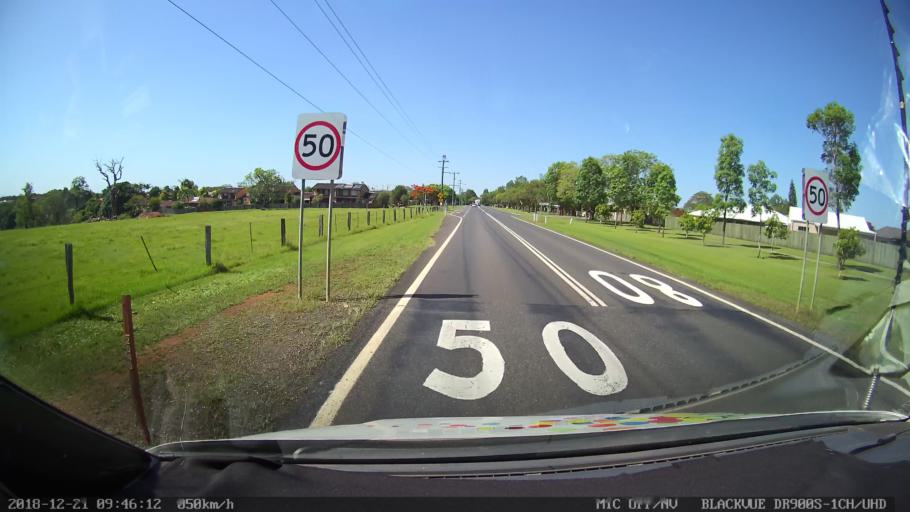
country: AU
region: New South Wales
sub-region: Clarence Valley
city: Grafton
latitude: -29.6365
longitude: 152.9268
